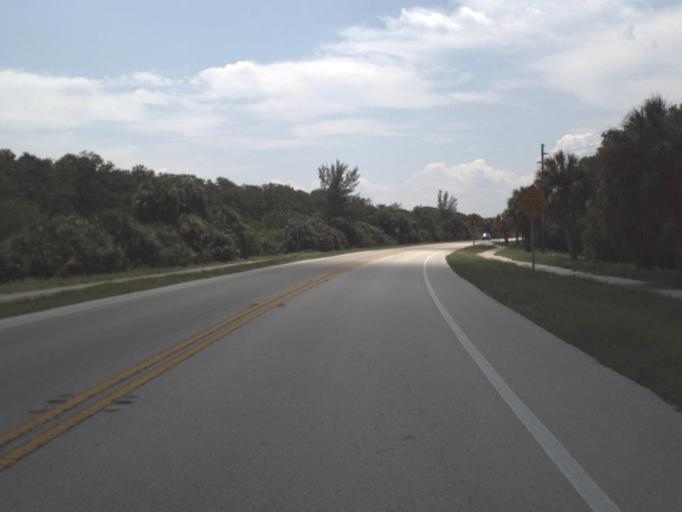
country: US
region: Florida
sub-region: Pinellas County
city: Tierra Verde
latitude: 27.6578
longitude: -82.7195
